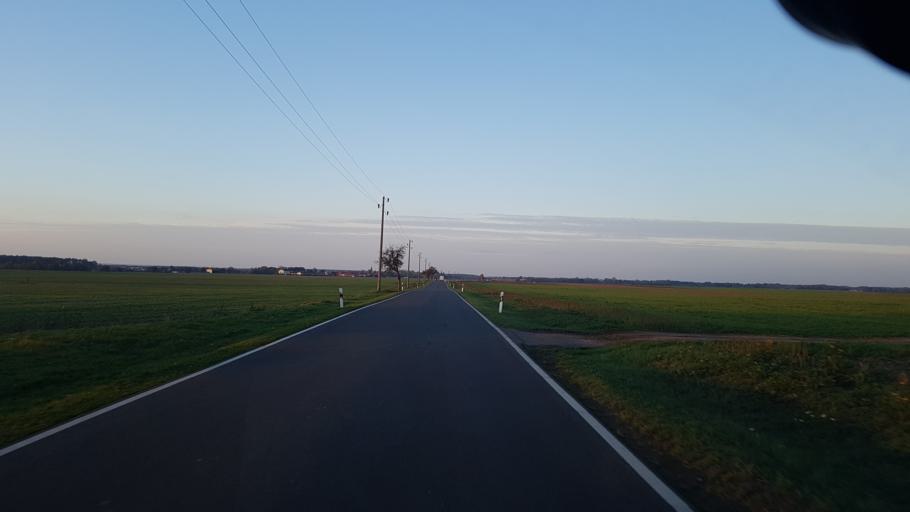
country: DE
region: Saxony
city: Schildau
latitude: 51.4792
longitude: 13.0055
